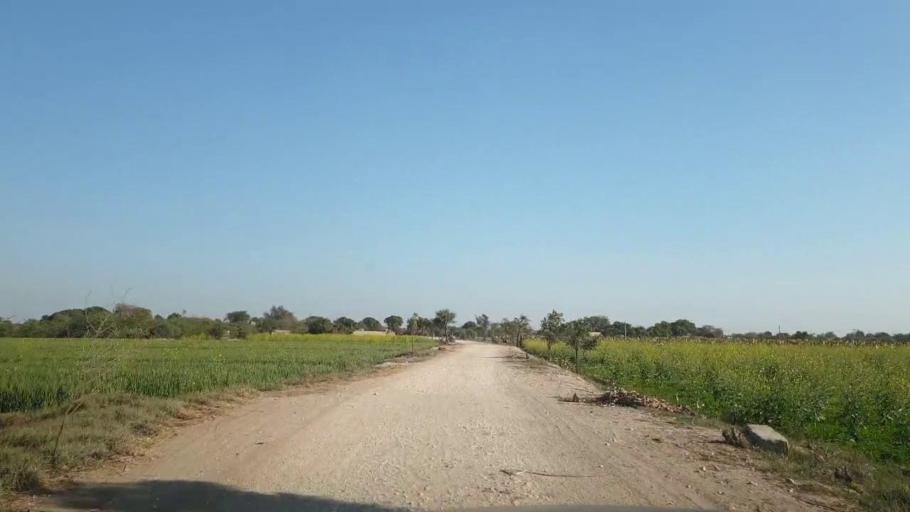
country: PK
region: Sindh
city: Tando Adam
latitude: 25.6902
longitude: 68.6874
